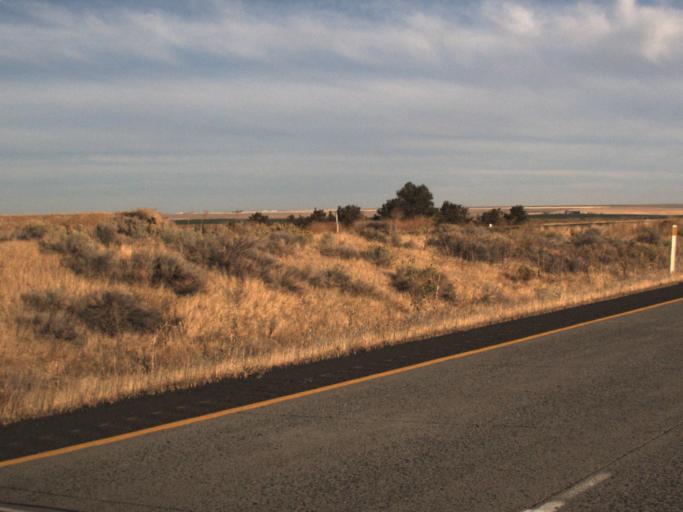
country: US
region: Washington
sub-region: Franklin County
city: Connell
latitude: 46.6949
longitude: -118.8367
